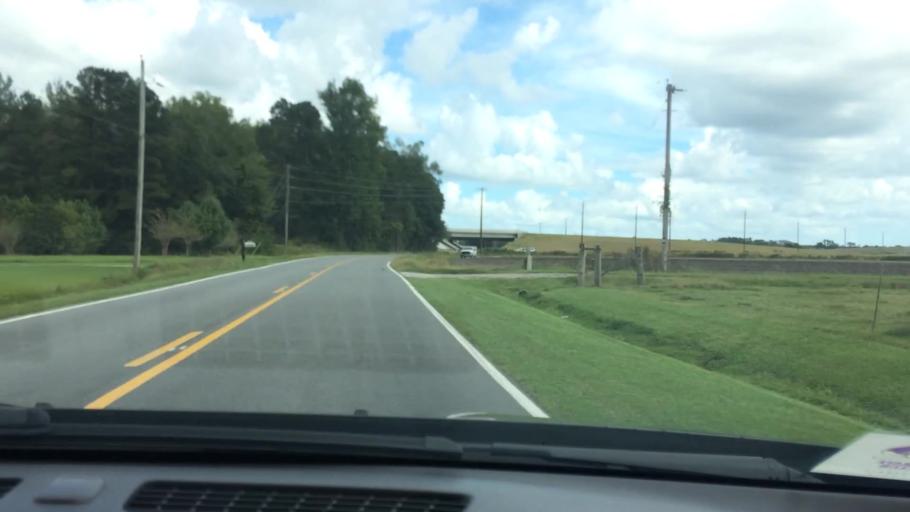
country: US
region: North Carolina
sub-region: Pitt County
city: Ayden
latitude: 35.4670
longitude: -77.4459
